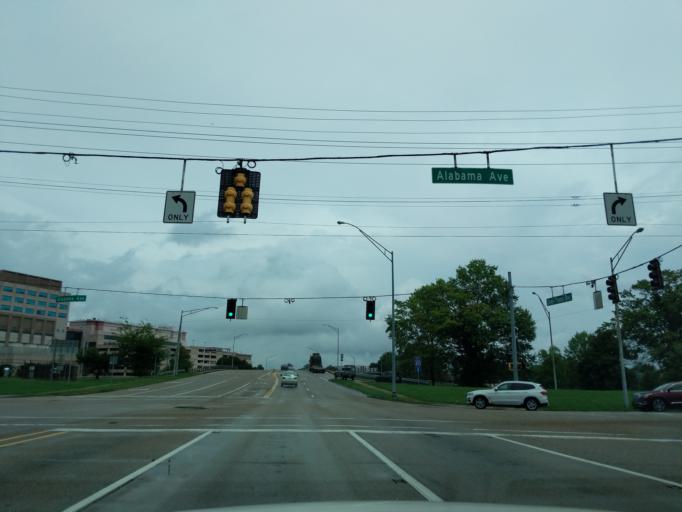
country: US
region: Tennessee
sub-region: Shelby County
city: Memphis
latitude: 35.1505
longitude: -90.0418
